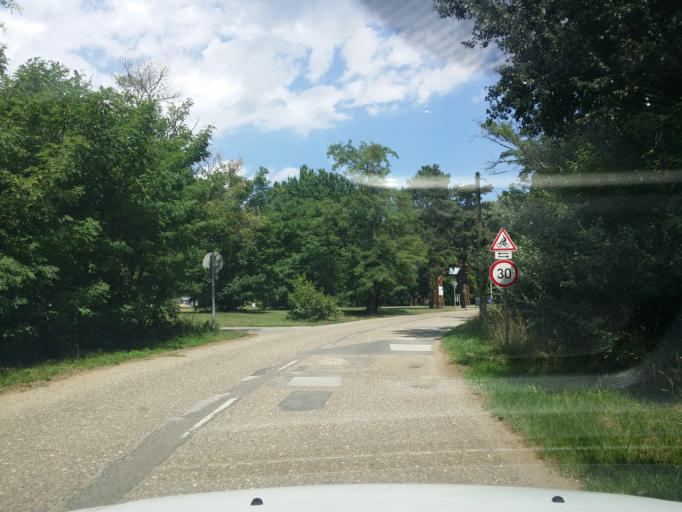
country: HU
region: Jasz-Nagykun-Szolnok
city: Tiszafured
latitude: 47.6217
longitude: 20.7373
